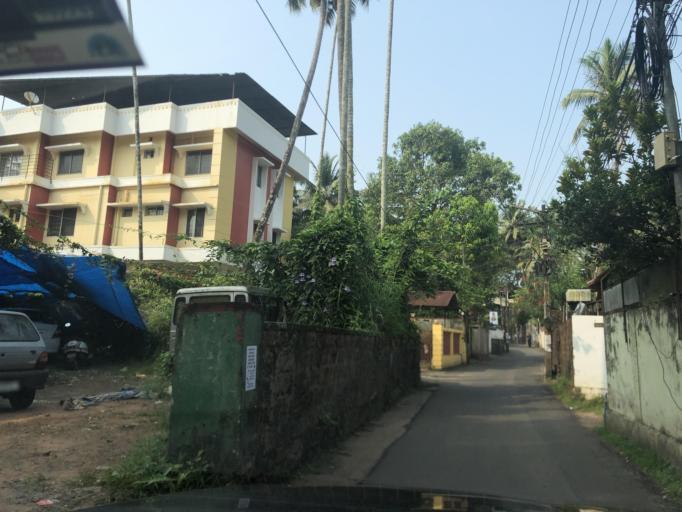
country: IN
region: Kerala
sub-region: Kozhikode
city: Kozhikode
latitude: 11.2776
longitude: 75.7785
